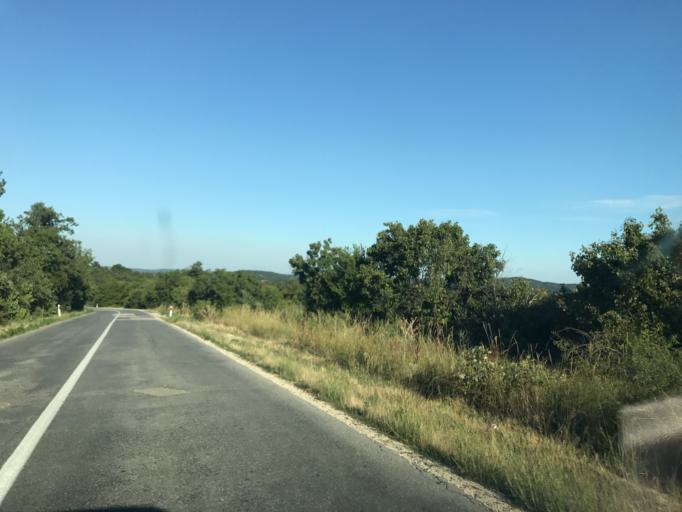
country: RO
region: Mehedinti
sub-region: Comuna Svinita
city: Svinita
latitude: 44.3034
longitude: 22.2428
